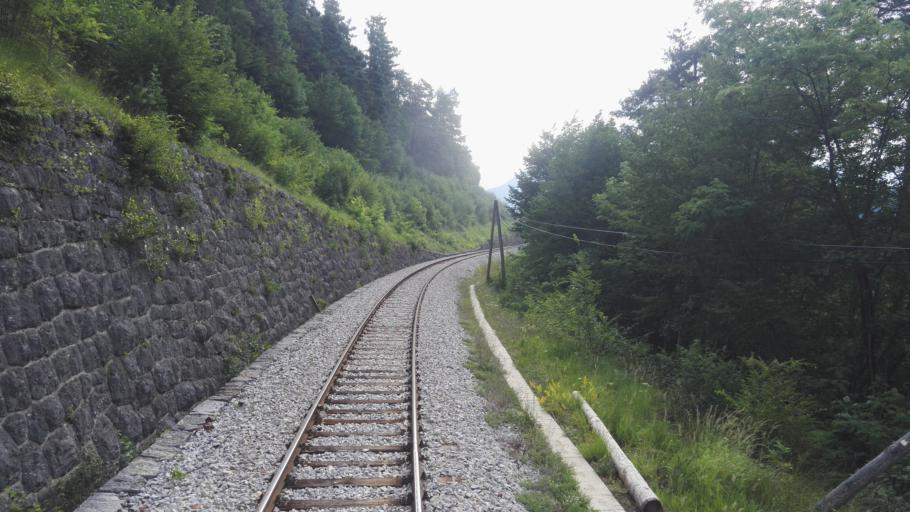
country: SI
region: Gorje
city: Zgornje Gorje
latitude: 46.3621
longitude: 14.0763
